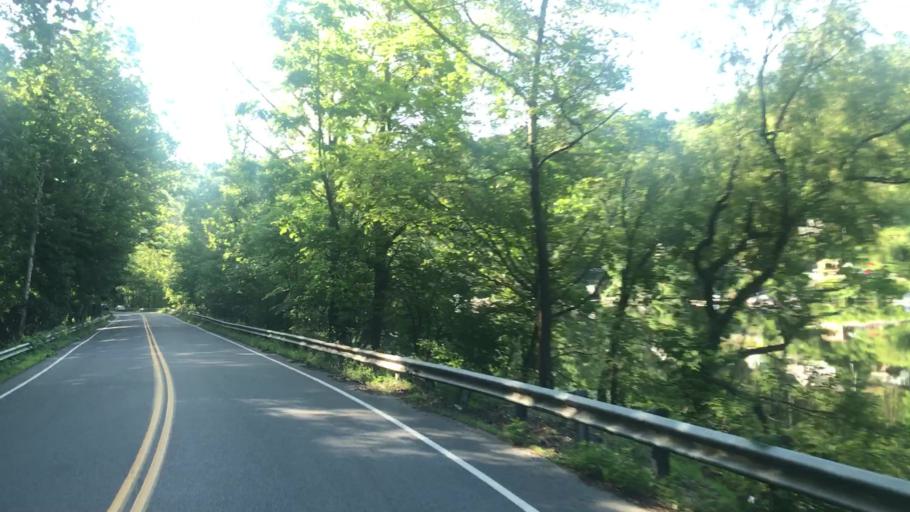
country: US
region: Connecticut
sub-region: Fairfield County
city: Newtown
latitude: 41.4352
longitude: -73.2635
